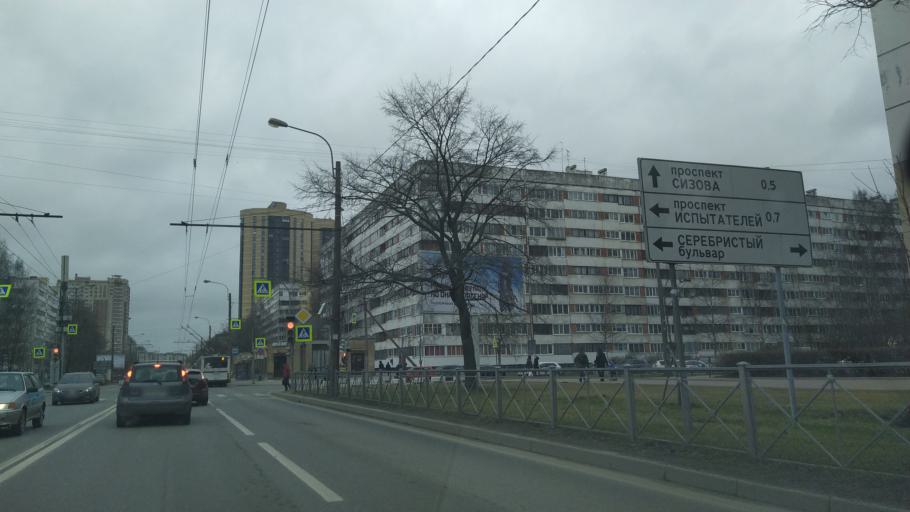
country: RU
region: St.-Petersburg
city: Komendantsky aerodrom
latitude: 60.0107
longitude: 30.2853
